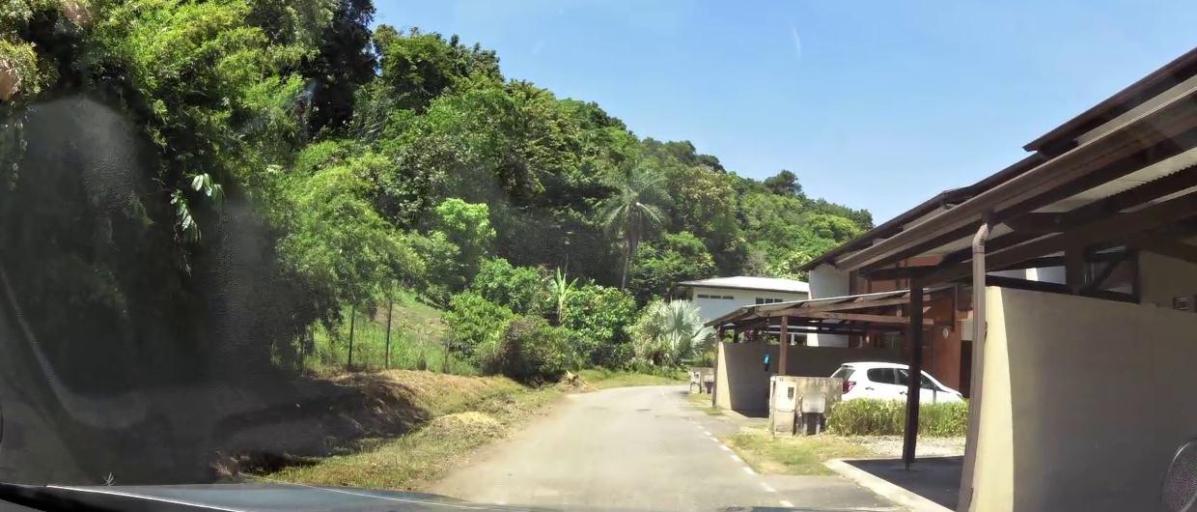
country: GF
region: Guyane
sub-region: Guyane
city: Remire-Montjoly
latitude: 4.9227
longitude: -52.2865
